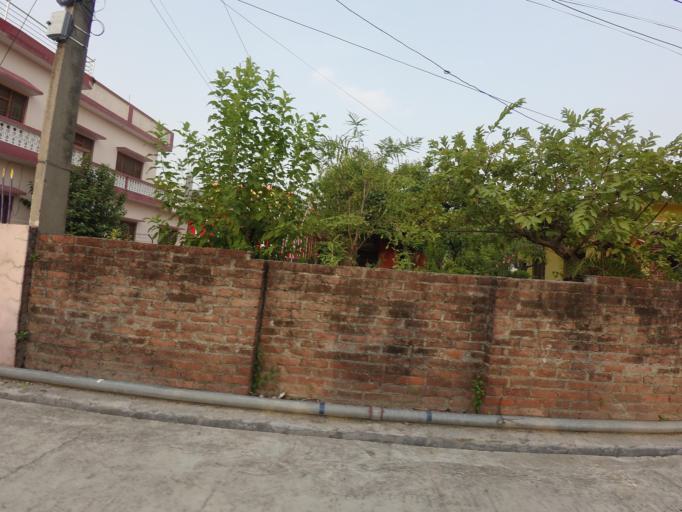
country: NP
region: Western Region
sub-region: Lumbini Zone
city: Bhairahawa
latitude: 27.5131
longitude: 83.4555
